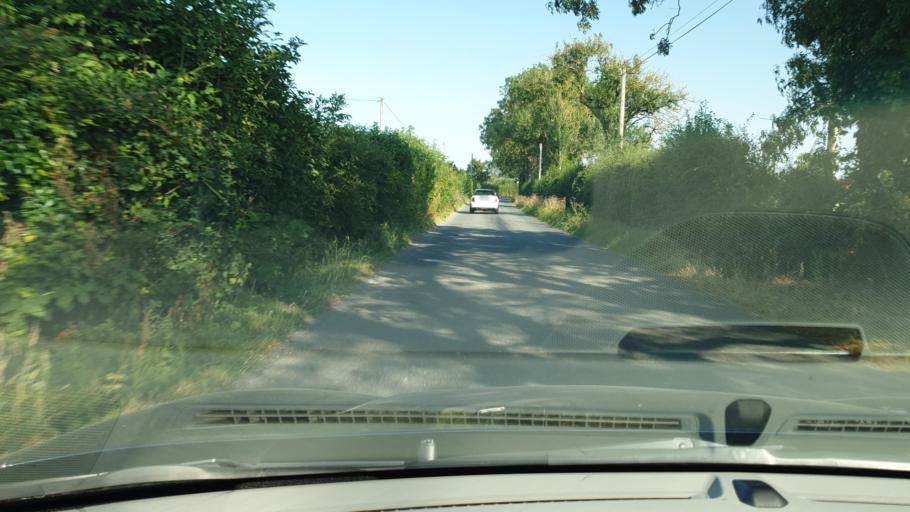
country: IE
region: Leinster
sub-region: An Mhi
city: Athboy
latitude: 53.6299
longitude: -6.9587
